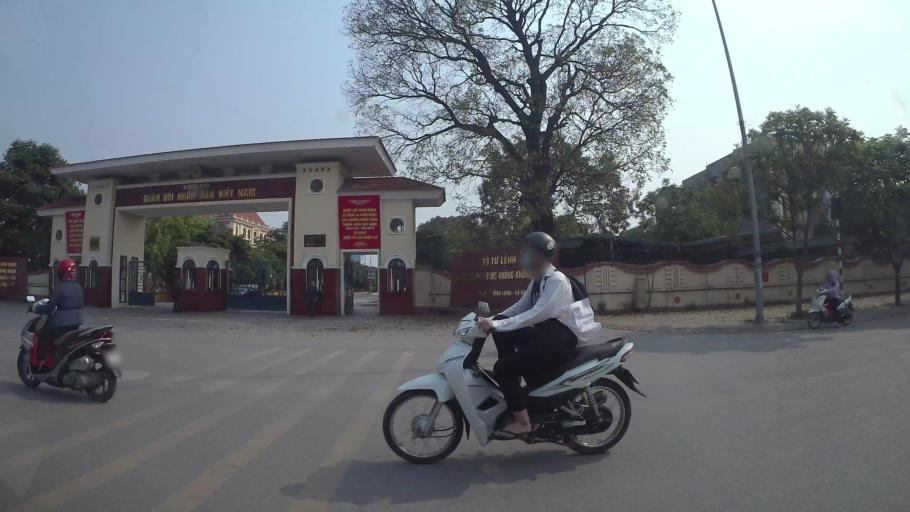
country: VN
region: Ha Noi
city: Dong Da
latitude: 20.9998
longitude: 105.8318
